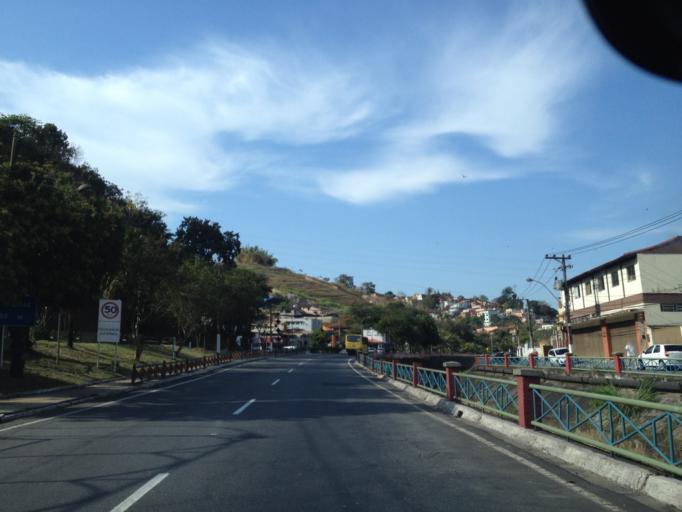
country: BR
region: Rio de Janeiro
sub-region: Volta Redonda
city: Volta Redonda
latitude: -22.5275
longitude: -44.1161
